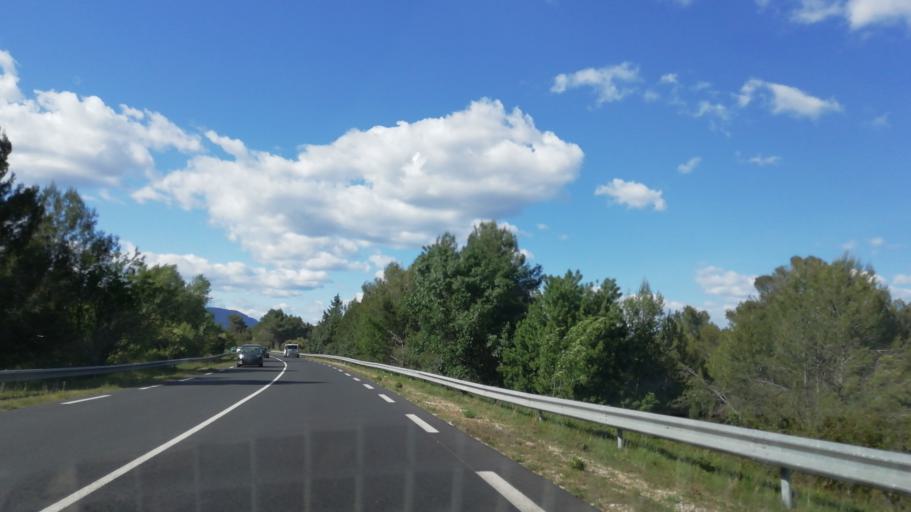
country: FR
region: Languedoc-Roussillon
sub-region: Departement de l'Herault
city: Saint-Clement-de-Riviere
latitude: 43.6946
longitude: 3.8266
